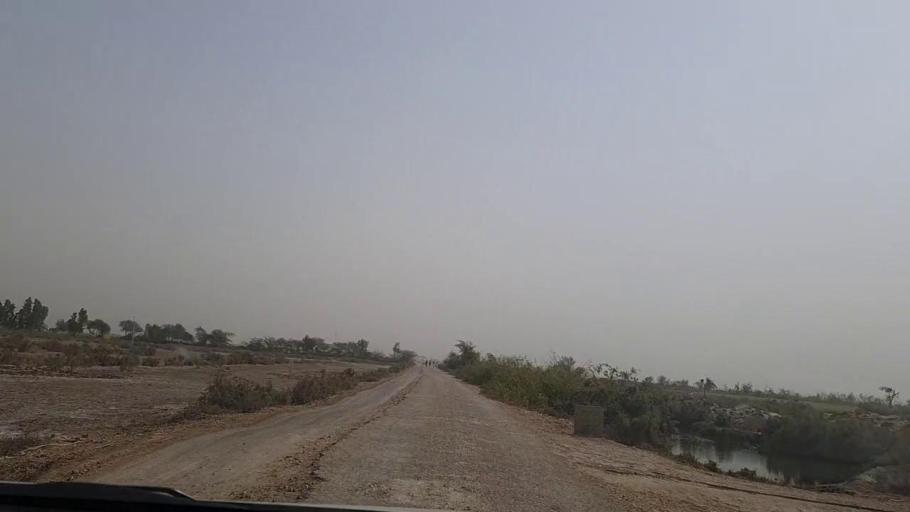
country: PK
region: Sindh
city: Pithoro
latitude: 25.4620
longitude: 69.2286
